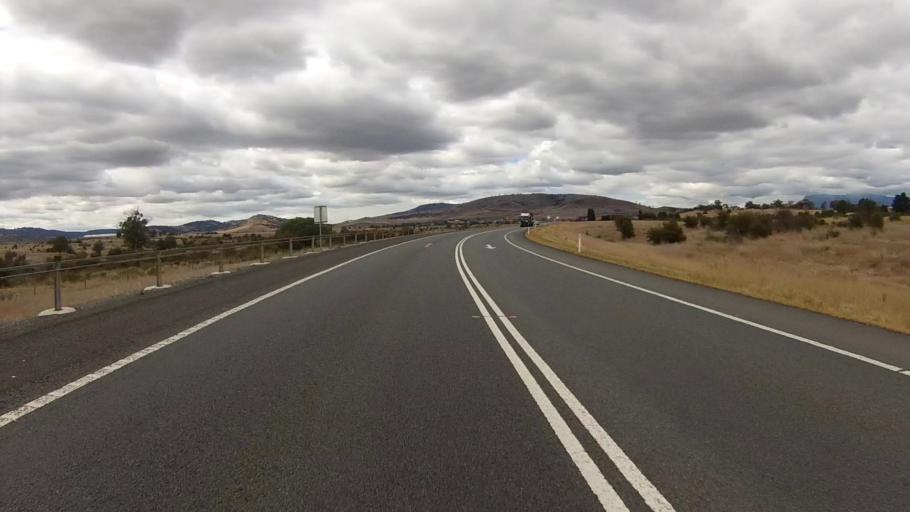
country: AU
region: Tasmania
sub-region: Brighton
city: Bridgewater
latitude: -42.6729
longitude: 147.2690
